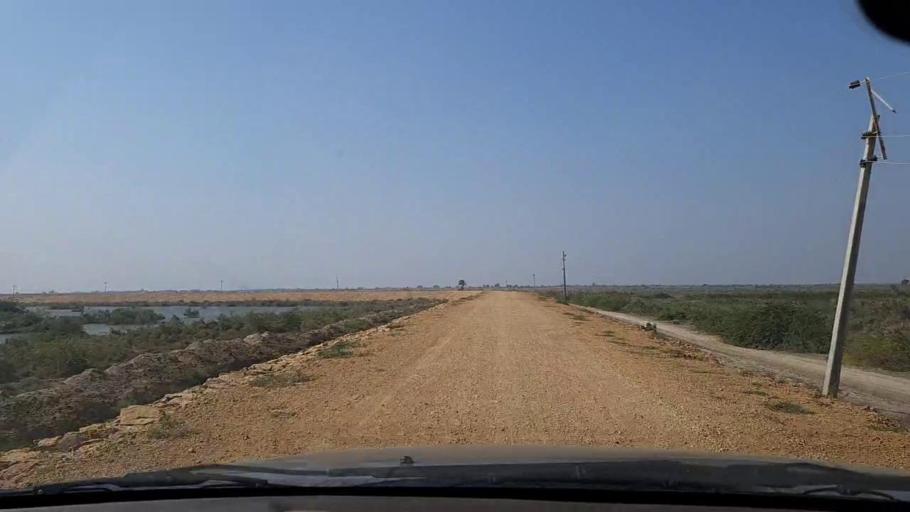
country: PK
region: Sindh
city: Chuhar Jamali
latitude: 24.4625
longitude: 67.8828
